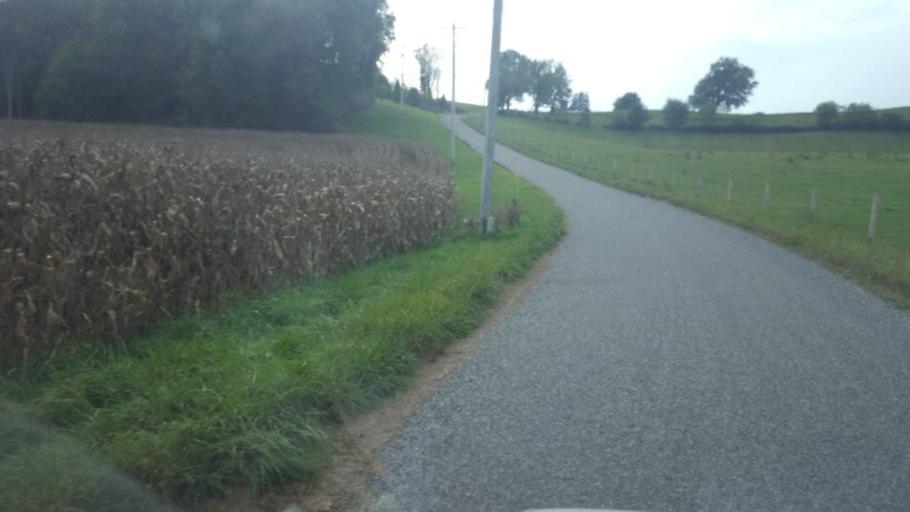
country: US
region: Ohio
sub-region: Holmes County
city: Millersburg
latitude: 40.5863
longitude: -81.8368
